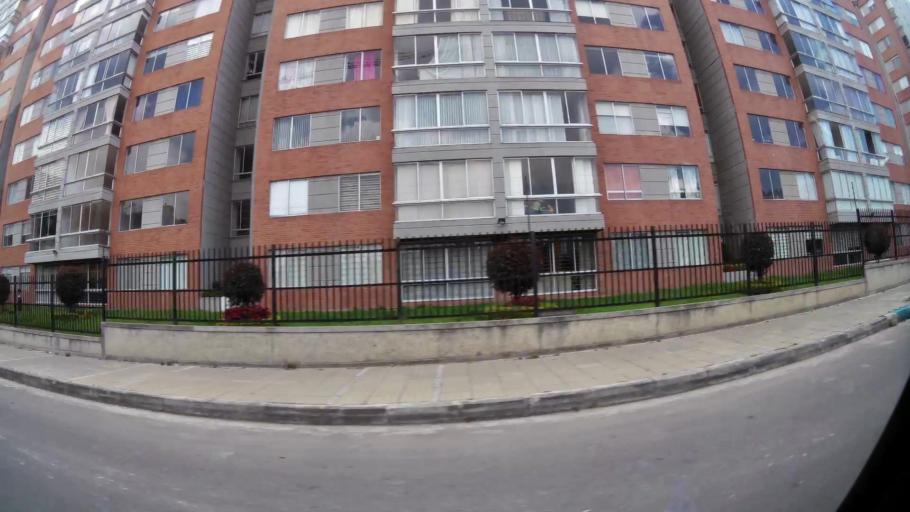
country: CO
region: Cundinamarca
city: La Calera
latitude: 4.7451
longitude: -74.0262
